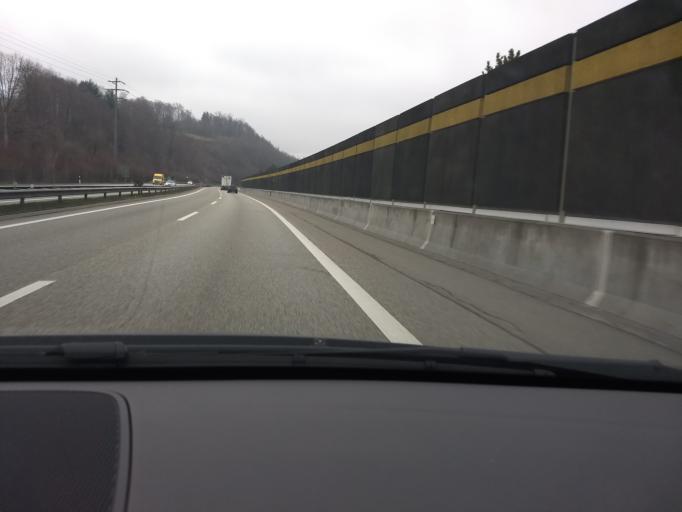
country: CH
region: Basel-Landschaft
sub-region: Bezirk Waldenburg
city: Diegten
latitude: 47.4145
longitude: 7.8093
